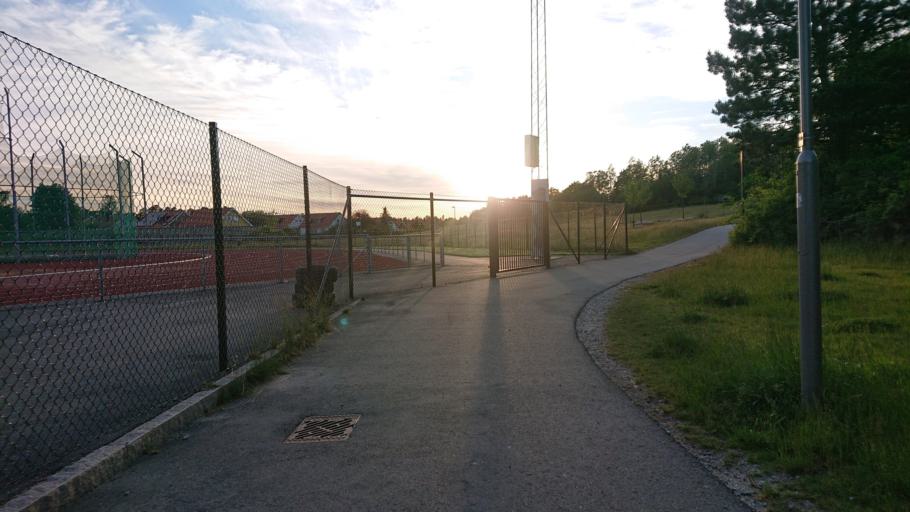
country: SE
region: Stockholm
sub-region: Osterakers Kommun
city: Akersberga
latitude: 59.4884
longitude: 18.3006
